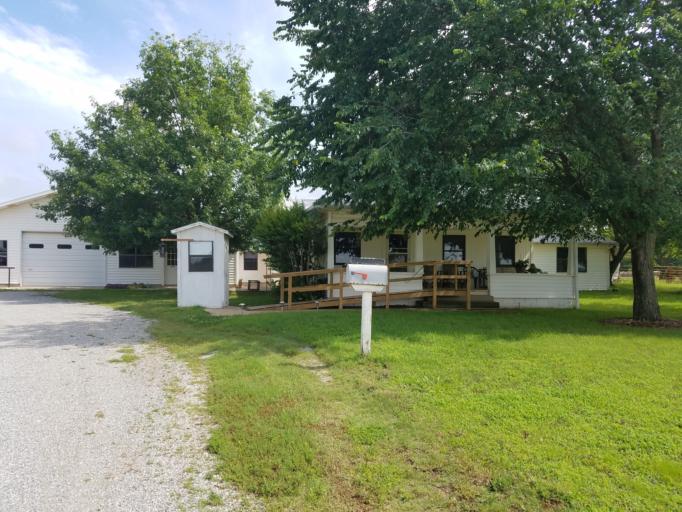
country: US
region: Oklahoma
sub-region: Coal County
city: Coalgate
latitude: 34.4331
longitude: -96.4350
